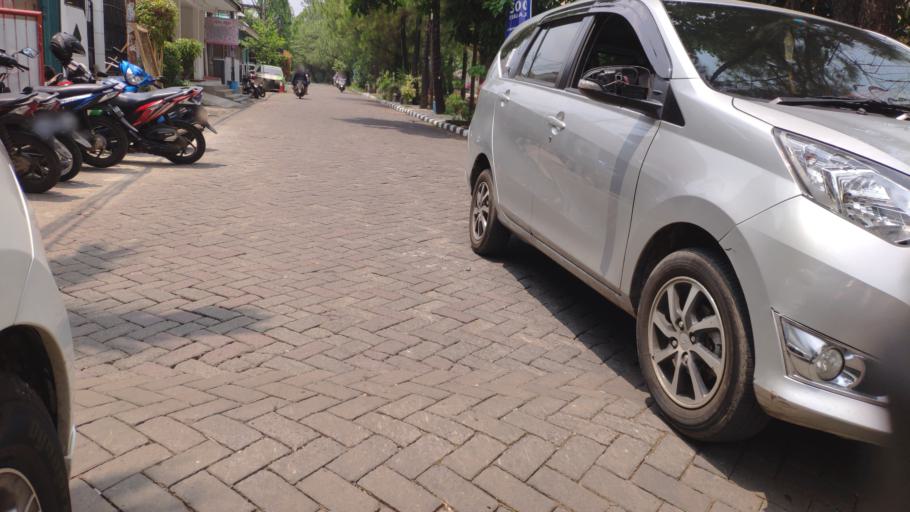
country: ID
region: West Java
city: Sawangan
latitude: -6.3991
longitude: 106.7935
